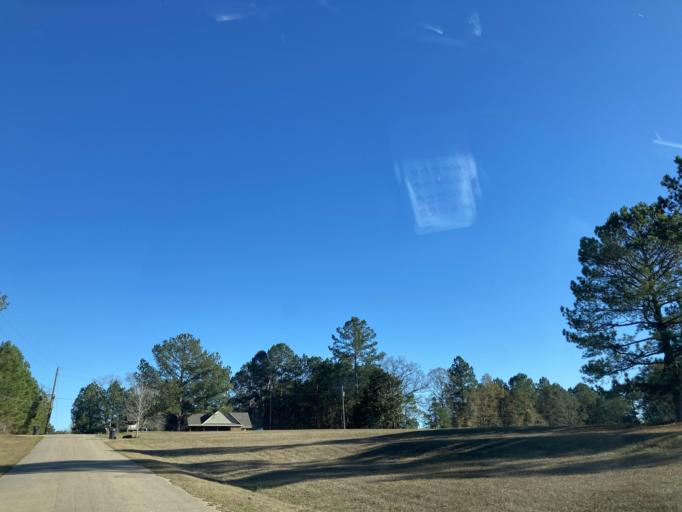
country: US
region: Mississippi
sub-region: Lamar County
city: Sumrall
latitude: 31.3764
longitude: -89.5999
